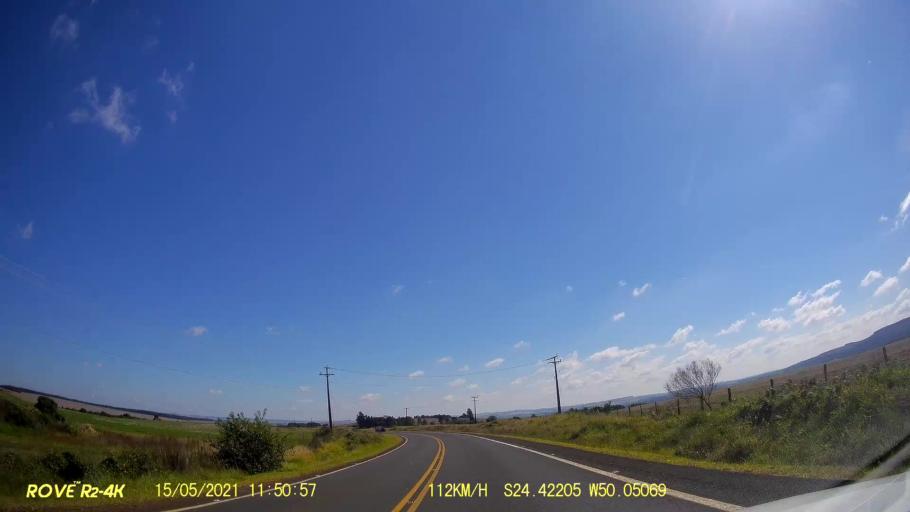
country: BR
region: Parana
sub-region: Pirai Do Sul
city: Pirai do Sul
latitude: -24.4228
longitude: -50.0490
